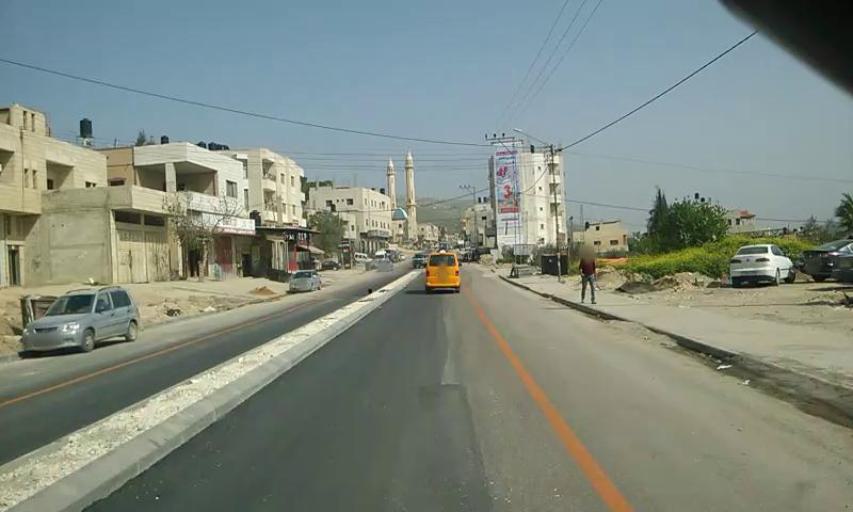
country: PS
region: West Bank
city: Huwwarah
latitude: 32.1551
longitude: 35.2595
